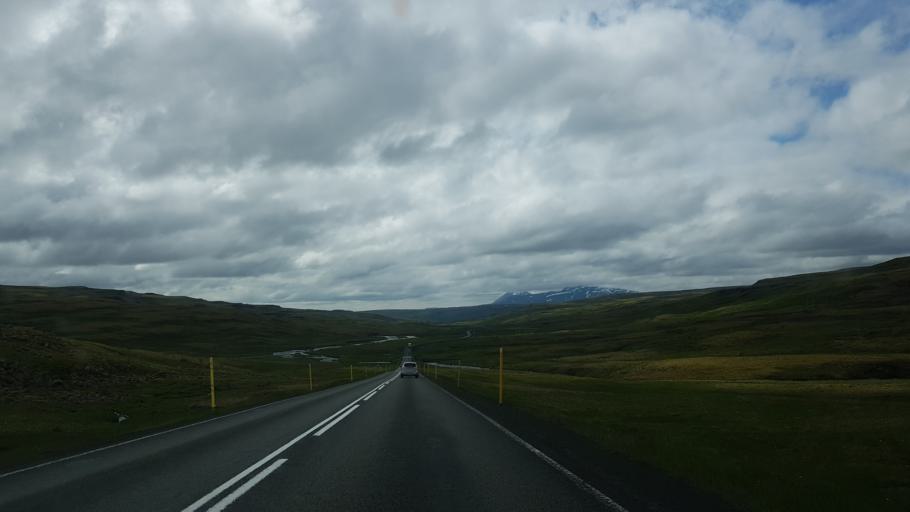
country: IS
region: West
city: Borgarnes
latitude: 64.9369
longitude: -21.0655
